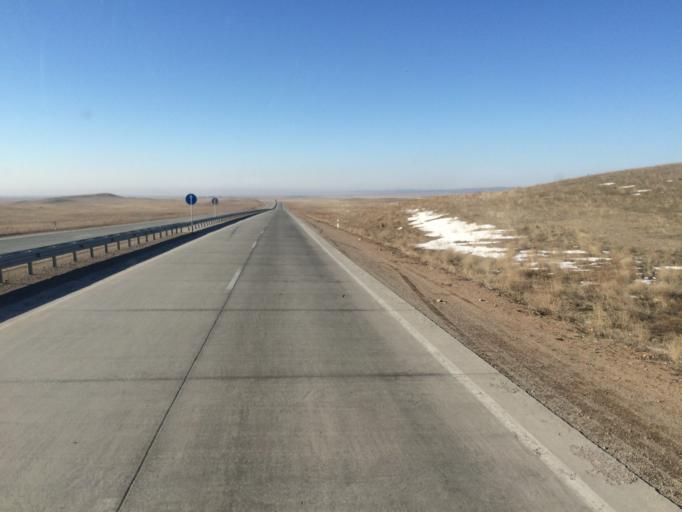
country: KZ
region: Zhambyl
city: Georgiyevka
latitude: 43.3395
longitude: 74.4612
